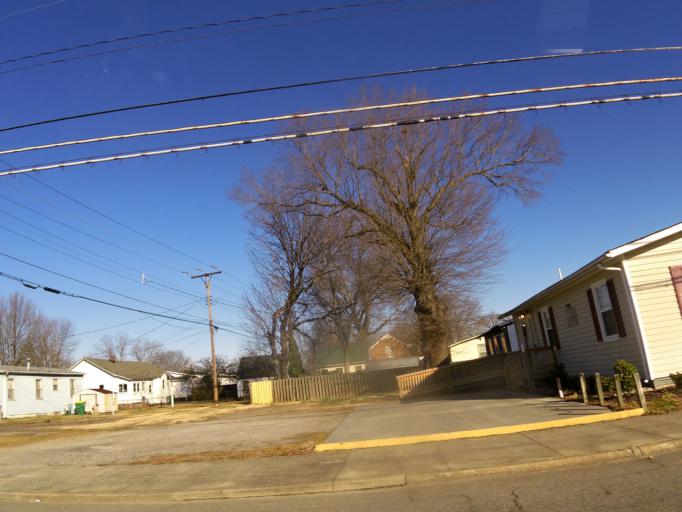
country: US
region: Virginia
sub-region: City of Hopewell
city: Hopewell
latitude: 37.3036
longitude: -77.2915
